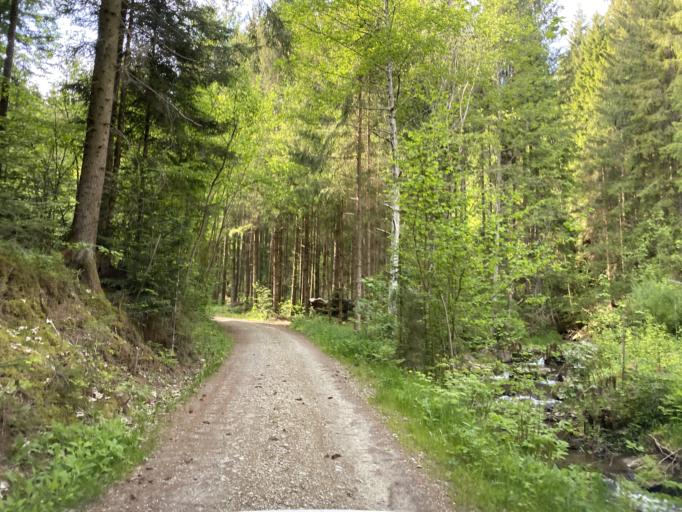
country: AT
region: Styria
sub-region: Politischer Bezirk Weiz
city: Birkfeld
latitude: 47.3602
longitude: 15.6866
